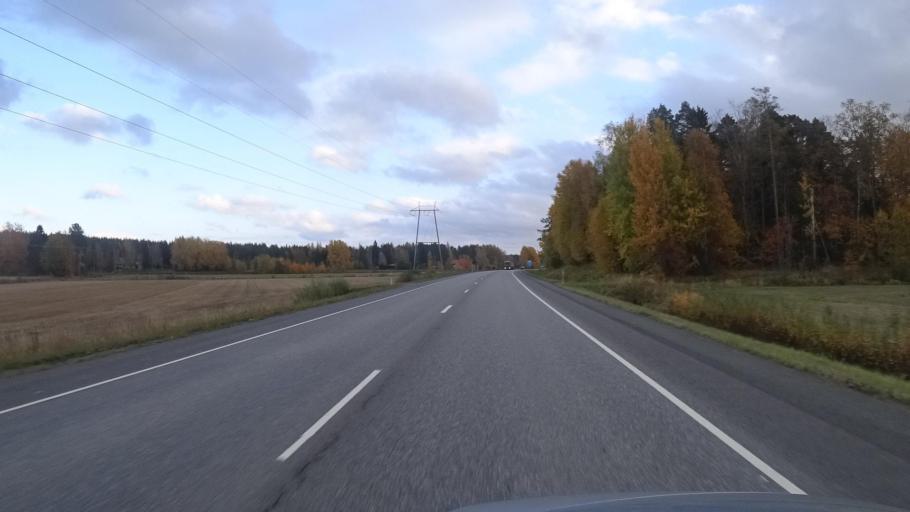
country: FI
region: Satakunta
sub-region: Rauma
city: Saekylae
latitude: 61.0262
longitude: 22.4024
